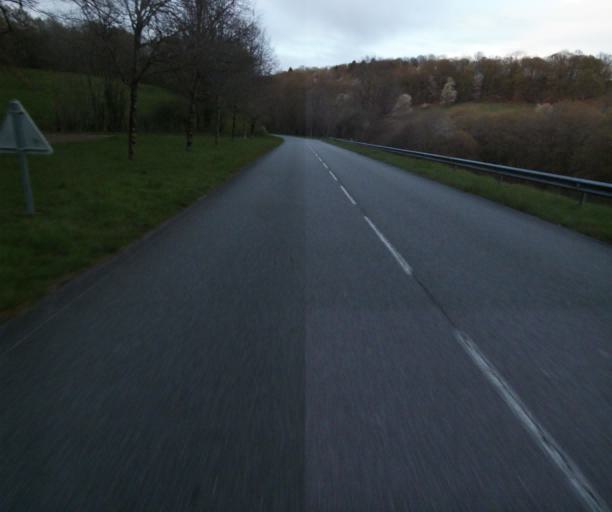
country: FR
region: Limousin
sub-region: Departement de la Correze
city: Laguenne
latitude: 45.2530
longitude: 1.8017
